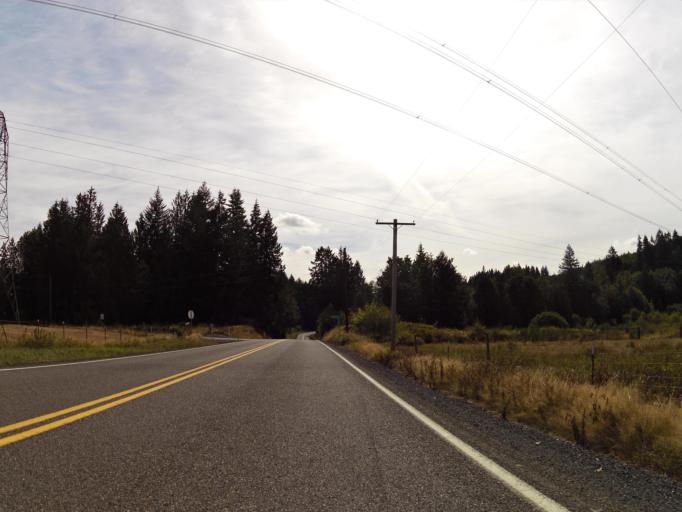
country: US
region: Washington
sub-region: Lewis County
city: Napavine
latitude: 46.5732
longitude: -122.9703
